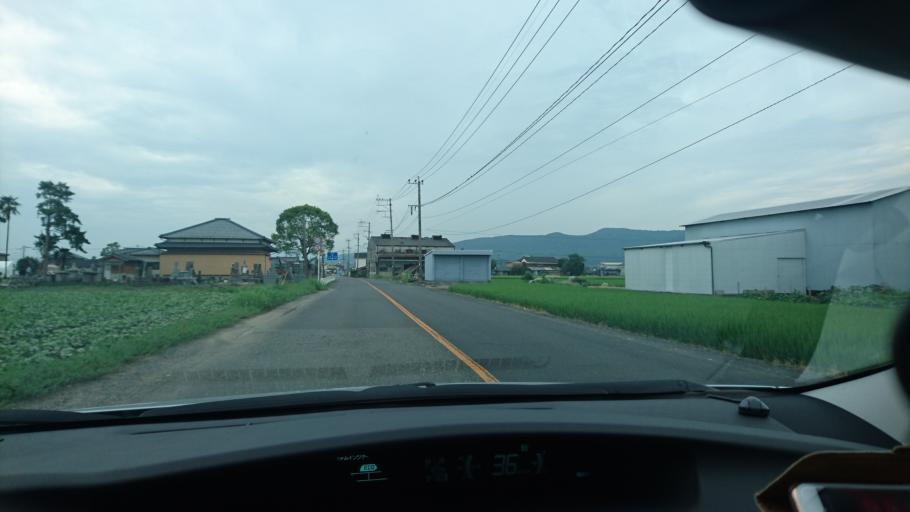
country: JP
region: Saga Prefecture
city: Kashima
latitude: 33.1969
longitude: 130.1148
